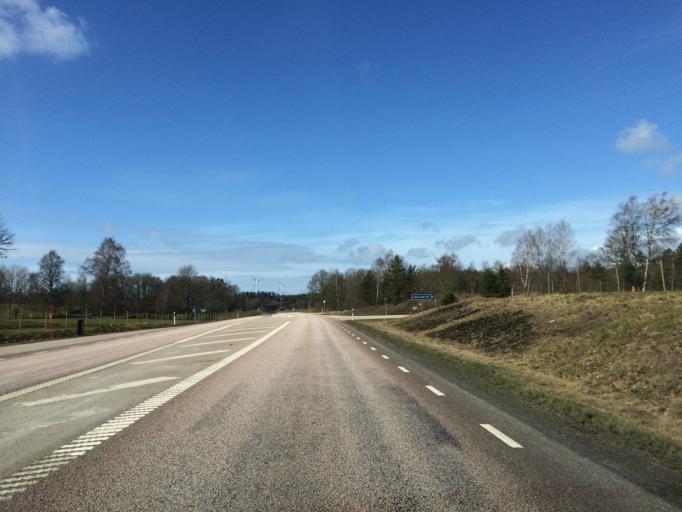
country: SE
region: Halland
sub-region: Laholms Kommun
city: Knared
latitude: 56.5247
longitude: 13.2484
